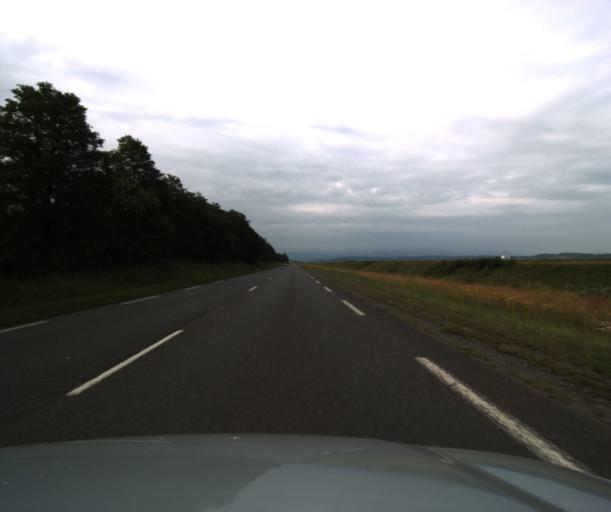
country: FR
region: Midi-Pyrenees
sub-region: Departement des Hautes-Pyrenees
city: Juillan
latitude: 43.2149
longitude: 0.0146
